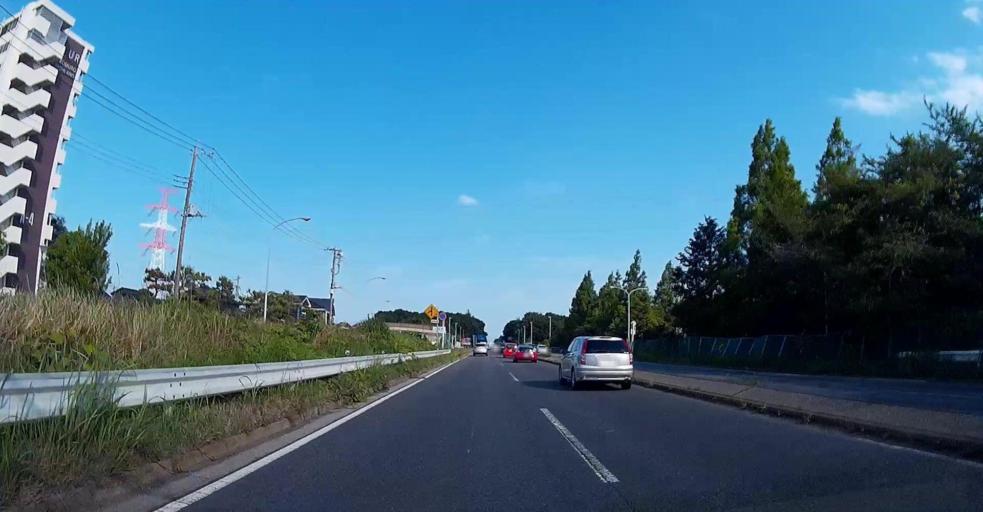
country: JP
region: Chiba
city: Shiroi
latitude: 35.7880
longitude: 140.0723
